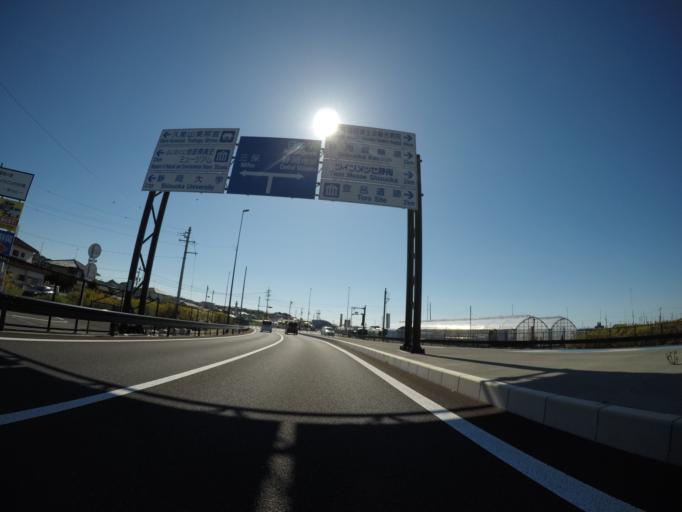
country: JP
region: Shizuoka
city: Shizuoka-shi
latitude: 34.9593
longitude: 138.4247
